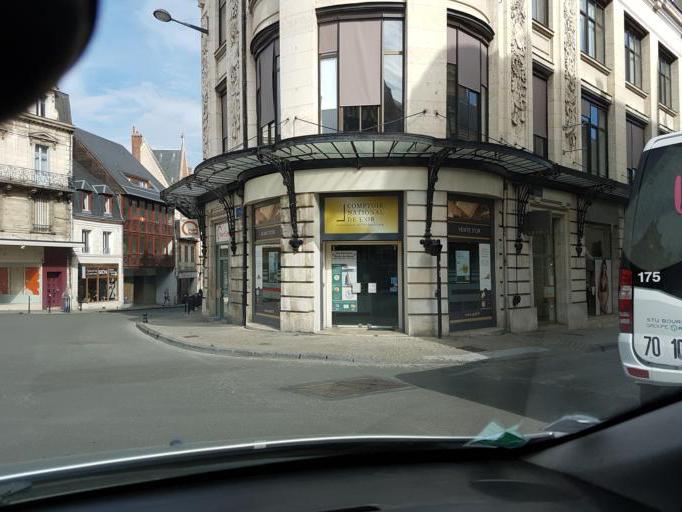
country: FR
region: Centre
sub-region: Departement du Cher
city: Bourges
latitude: 47.0859
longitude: 2.3937
